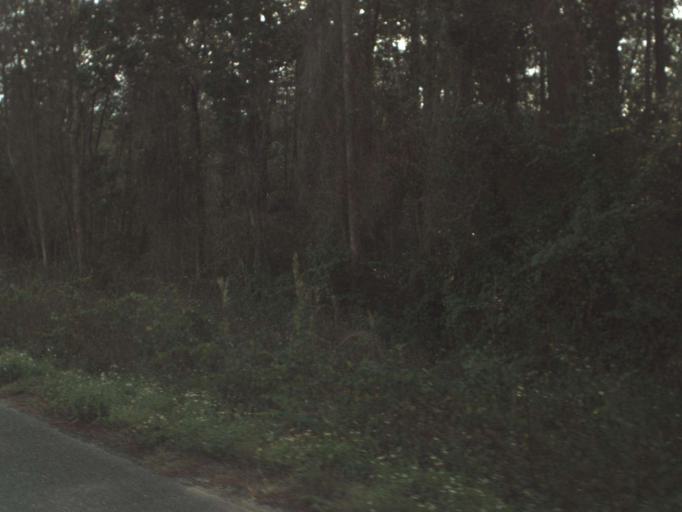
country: US
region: Florida
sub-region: Gulf County
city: Wewahitchka
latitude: 29.9943
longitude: -84.9769
